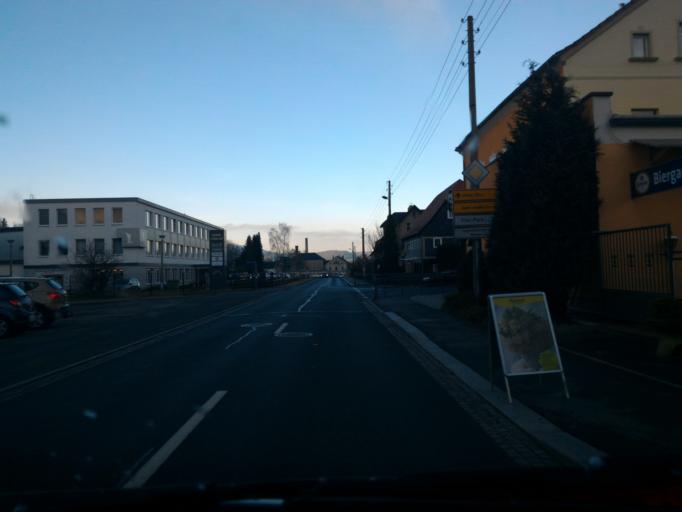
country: DE
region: Saxony
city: Grossschonau
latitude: 50.8884
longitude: 14.6597
